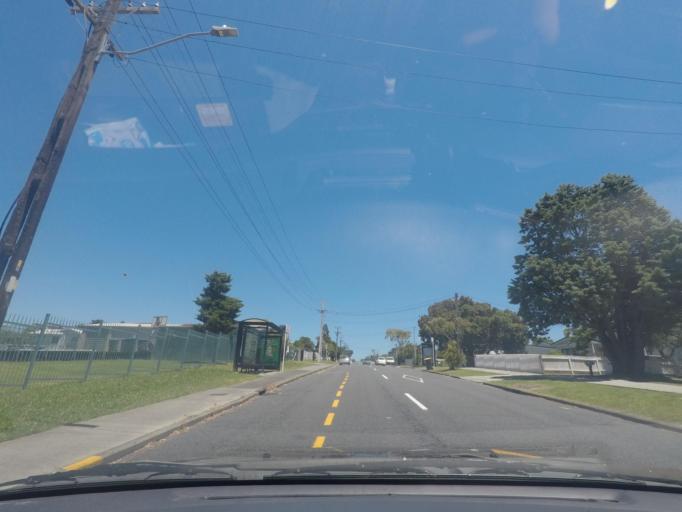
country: NZ
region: Auckland
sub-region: Auckland
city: Waitakere
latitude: -36.9179
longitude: 174.7147
